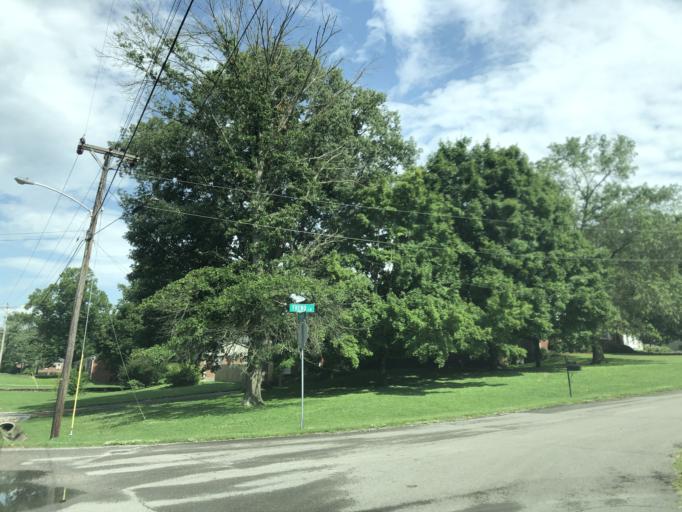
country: US
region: Tennessee
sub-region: Davidson County
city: Lakewood
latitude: 36.1792
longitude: -86.6766
